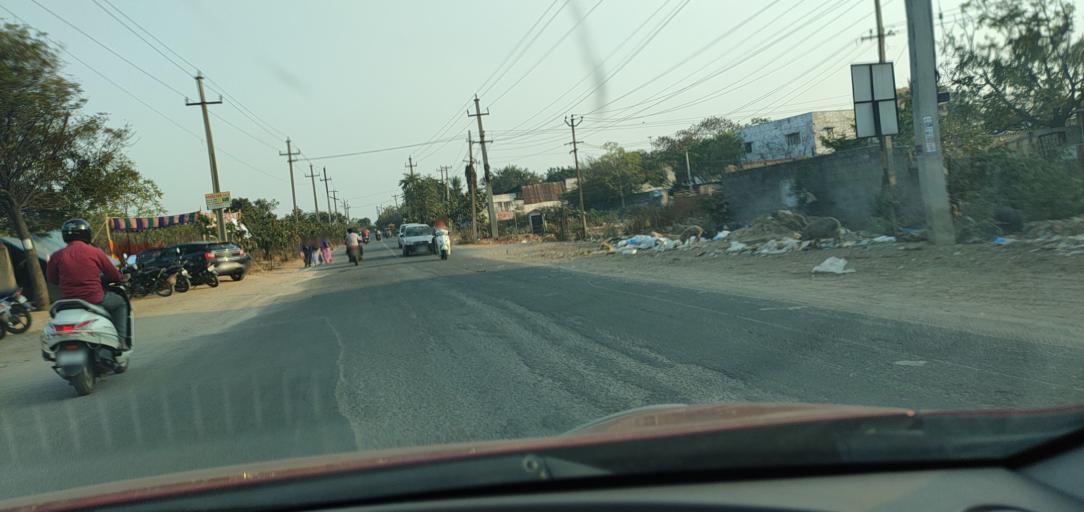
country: IN
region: Telangana
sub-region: Rangareddi
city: Uppal Kalan
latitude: 17.4331
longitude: 78.5778
